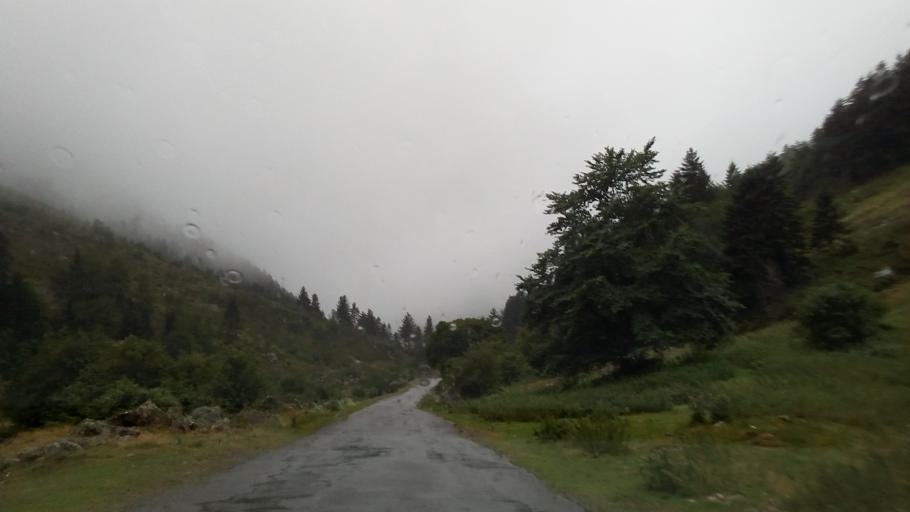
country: ES
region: Aragon
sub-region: Provincia de Huesca
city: Sallent de Gallego
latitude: 42.8970
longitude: -0.2669
